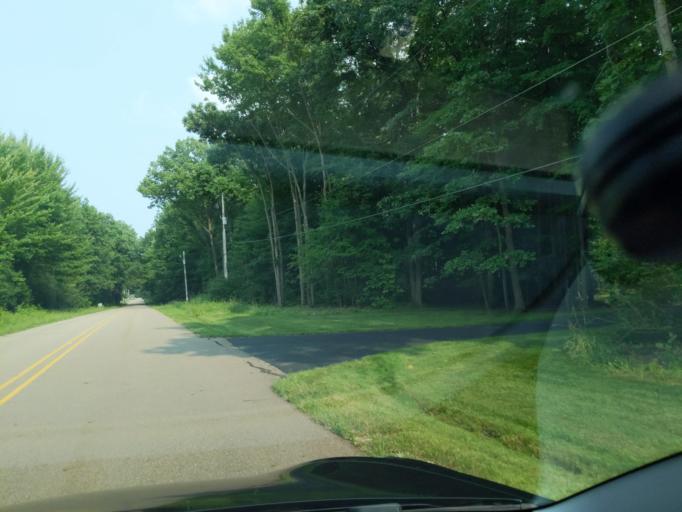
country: US
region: Michigan
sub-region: Jackson County
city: Spring Arbor
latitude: 42.2621
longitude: -84.4950
